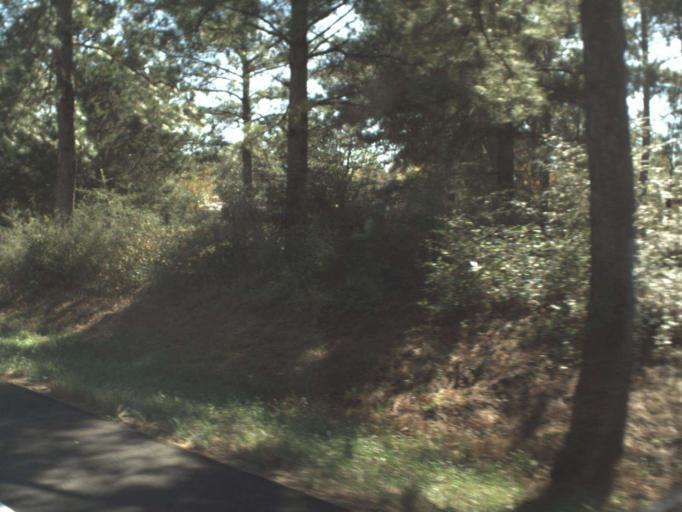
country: US
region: Alabama
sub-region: Escambia County
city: East Brewton
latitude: 30.8962
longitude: -86.9897
